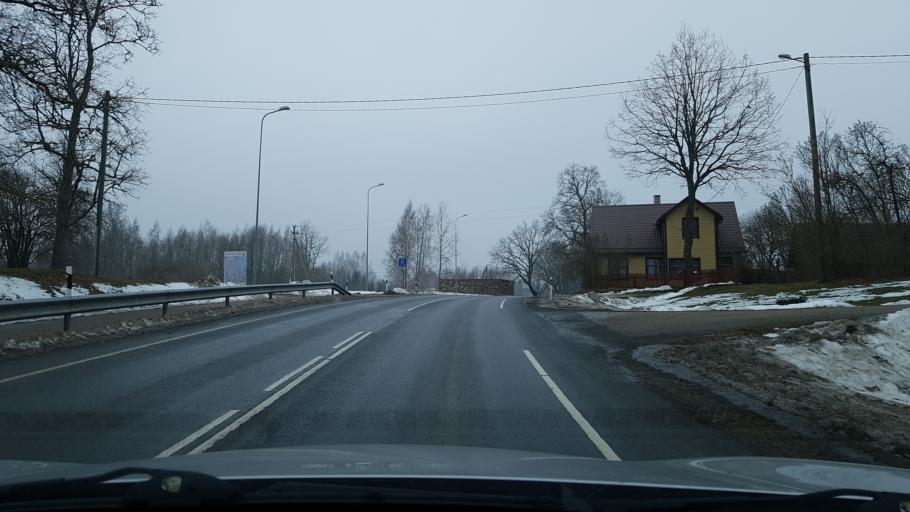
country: EE
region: Valgamaa
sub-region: Torva linn
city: Torva
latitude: 58.2300
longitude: 25.8830
